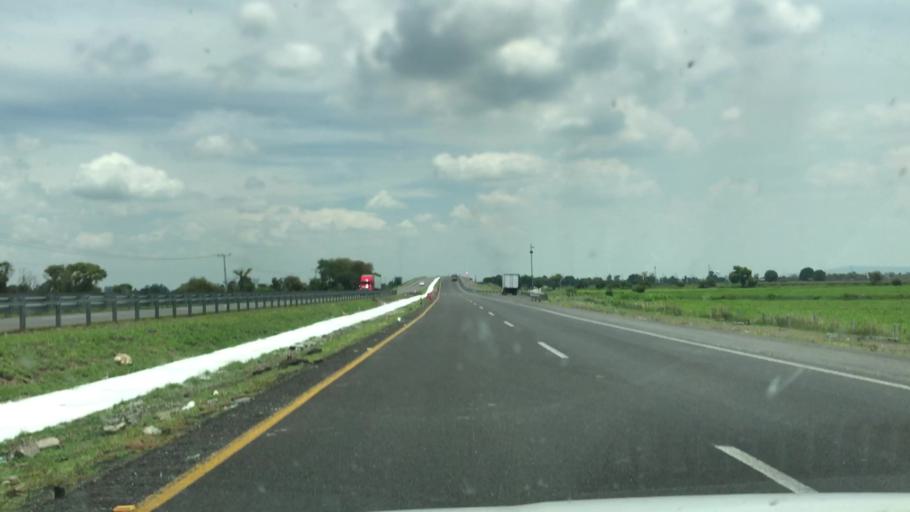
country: MX
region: Guanajuato
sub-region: Salamanca
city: San Vicente de Flores
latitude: 20.6109
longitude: -101.2195
